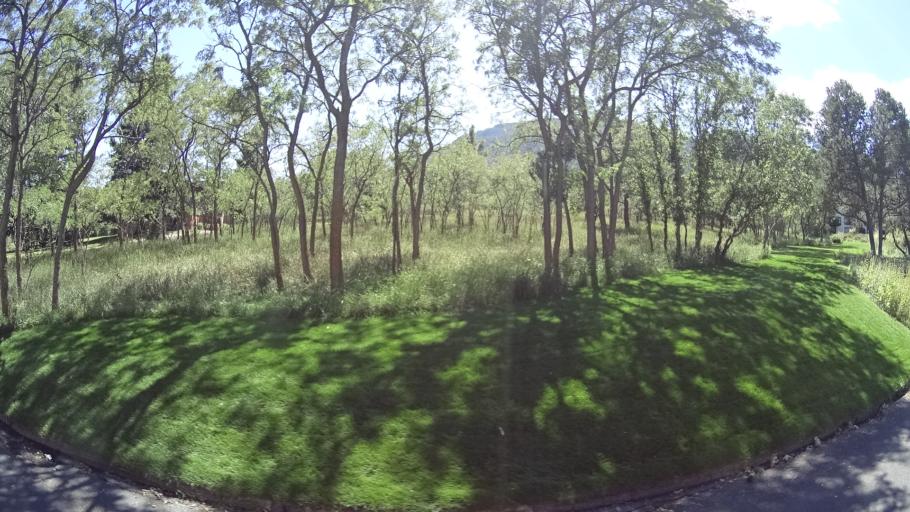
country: US
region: Colorado
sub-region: El Paso County
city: Colorado Springs
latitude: 38.7849
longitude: -104.8579
